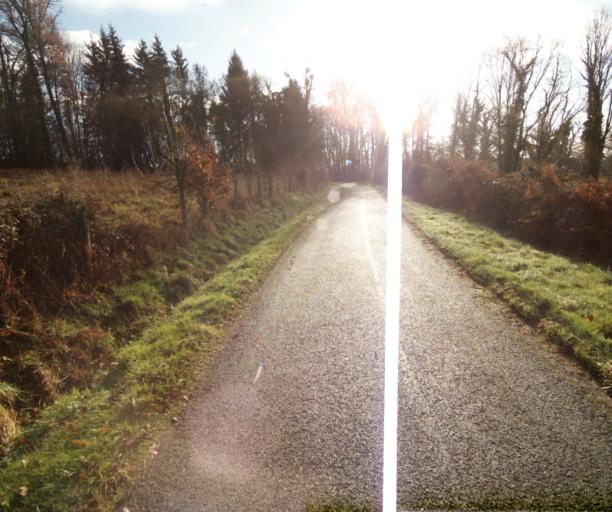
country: FR
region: Limousin
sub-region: Departement de la Correze
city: Sainte-Fereole
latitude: 45.2628
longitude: 1.5990
